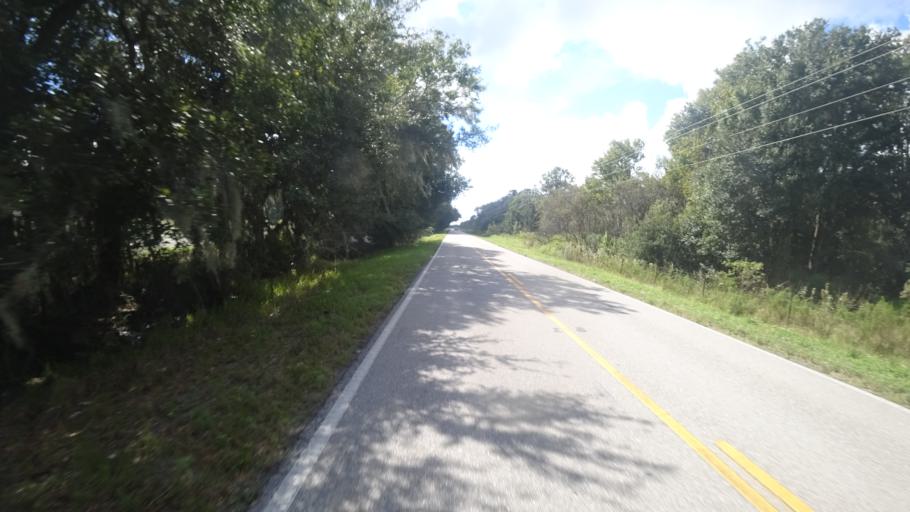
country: US
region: Florida
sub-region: Hillsborough County
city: Wimauma
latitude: 27.5562
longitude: -82.1038
